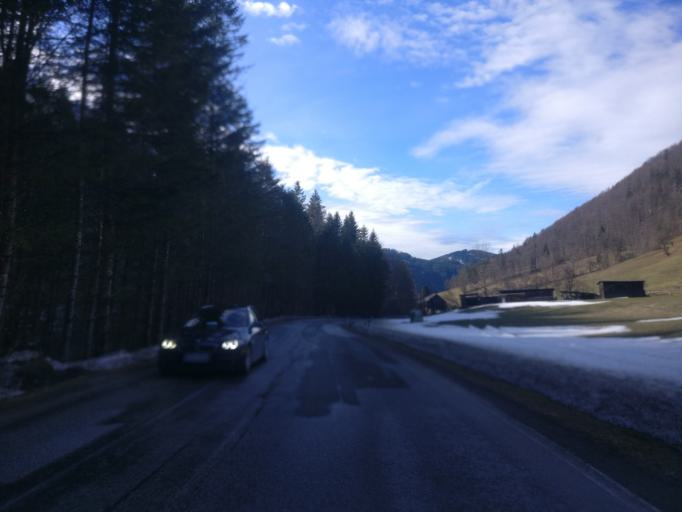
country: AT
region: Styria
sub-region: Politischer Bezirk Liezen
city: Altenmarkt bei Sankt Gallen
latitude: 47.6754
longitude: 14.6420
